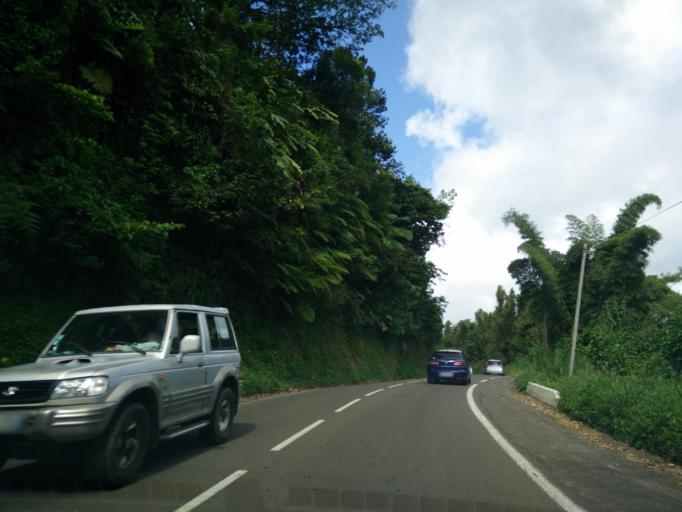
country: MQ
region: Martinique
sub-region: Martinique
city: Le Morne-Rouge
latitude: 14.7925
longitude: -61.1393
